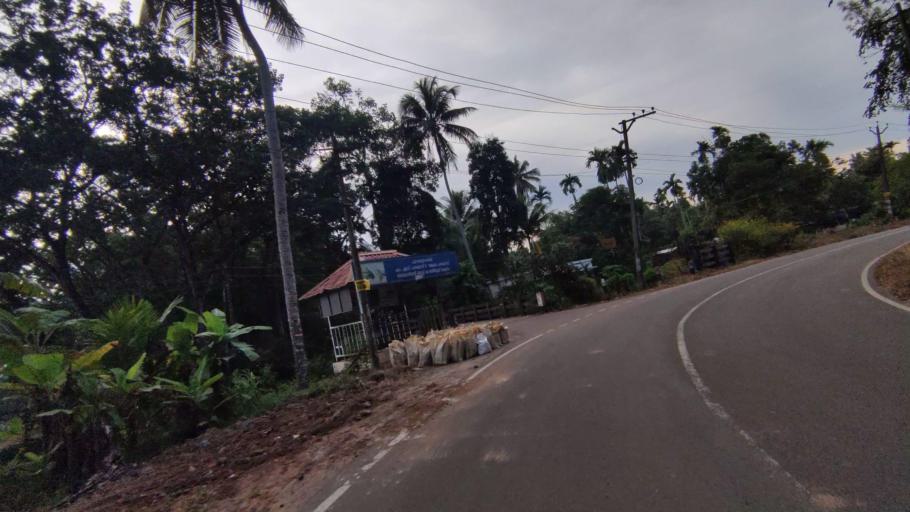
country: IN
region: Kerala
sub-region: Kottayam
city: Kottayam
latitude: 9.6389
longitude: 76.4882
